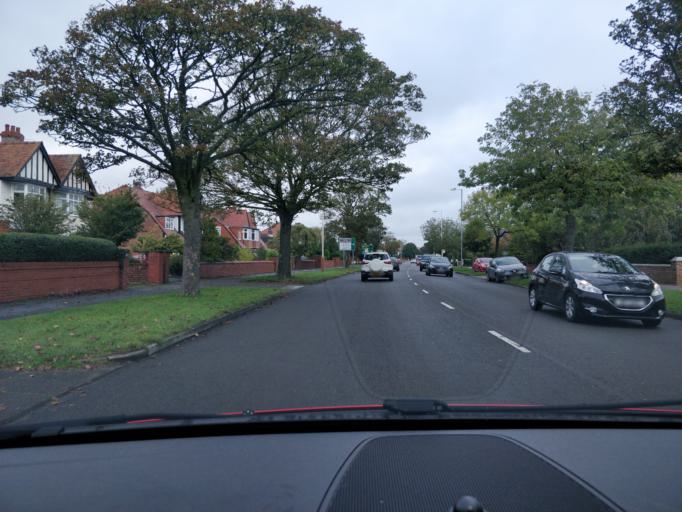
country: GB
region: England
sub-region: Sefton
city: Southport
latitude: 53.6110
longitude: -3.0222
